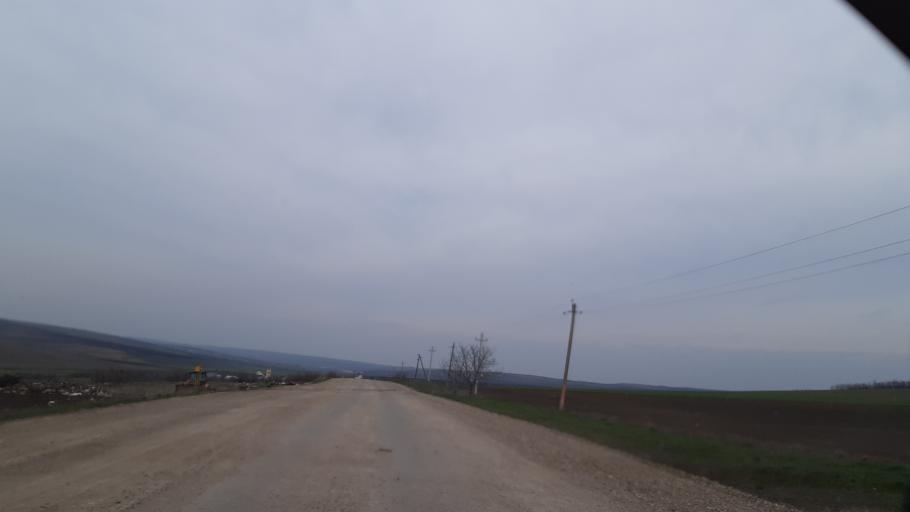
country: MD
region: Soldanesti
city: Soldanesti
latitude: 47.5942
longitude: 28.6490
